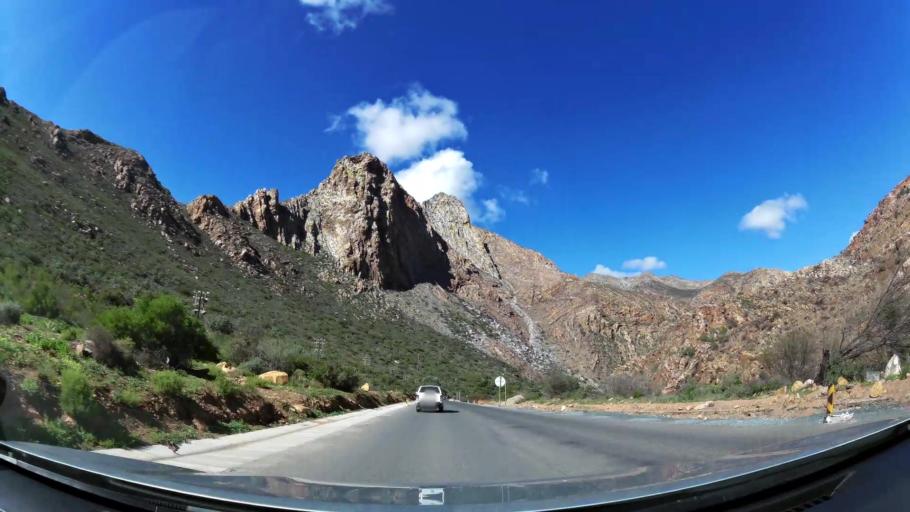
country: ZA
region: Western Cape
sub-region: Cape Winelands District Municipality
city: Ashton
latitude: -33.7979
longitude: 20.1038
